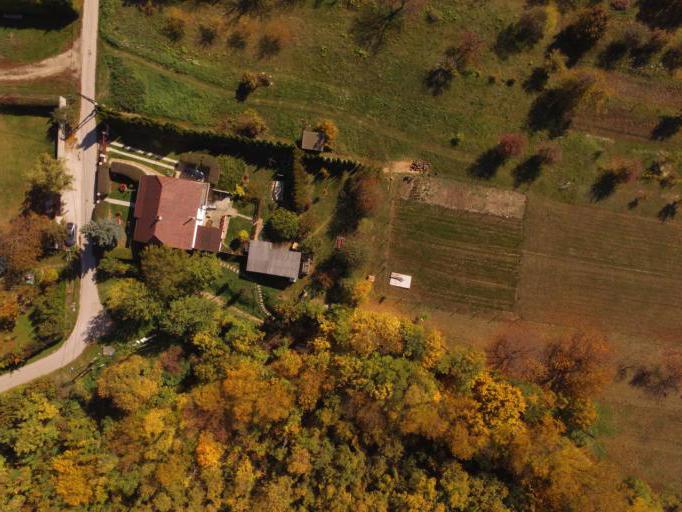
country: HU
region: Fejer
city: Many
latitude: 47.5208
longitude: 18.6171
